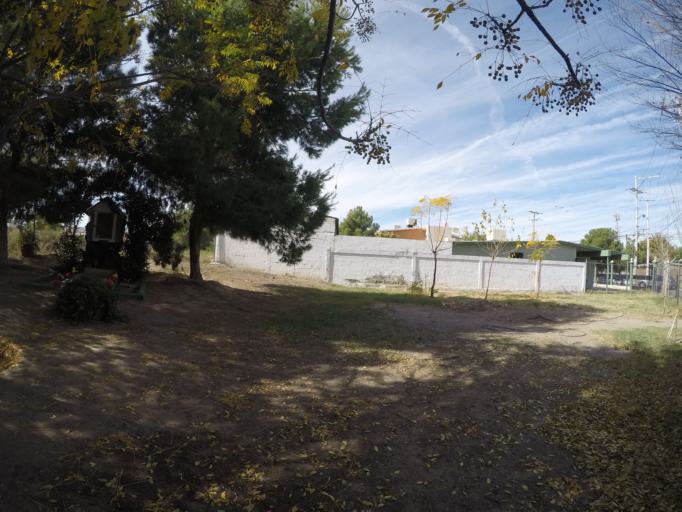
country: MX
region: Chihuahua
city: Ciudad Juarez
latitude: 31.7346
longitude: -106.4355
